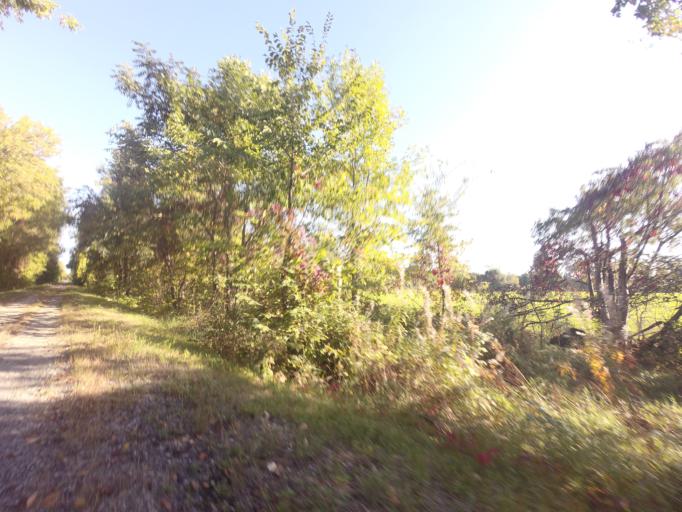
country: CA
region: Ontario
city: Hawkesbury
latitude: 45.5237
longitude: -74.5432
